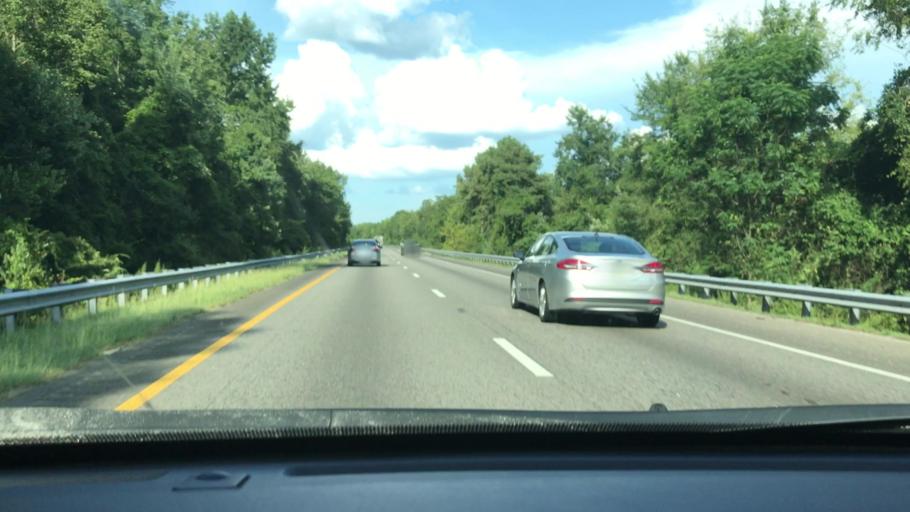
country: US
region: South Carolina
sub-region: Florence County
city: Florence
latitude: 34.2881
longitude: -79.6585
